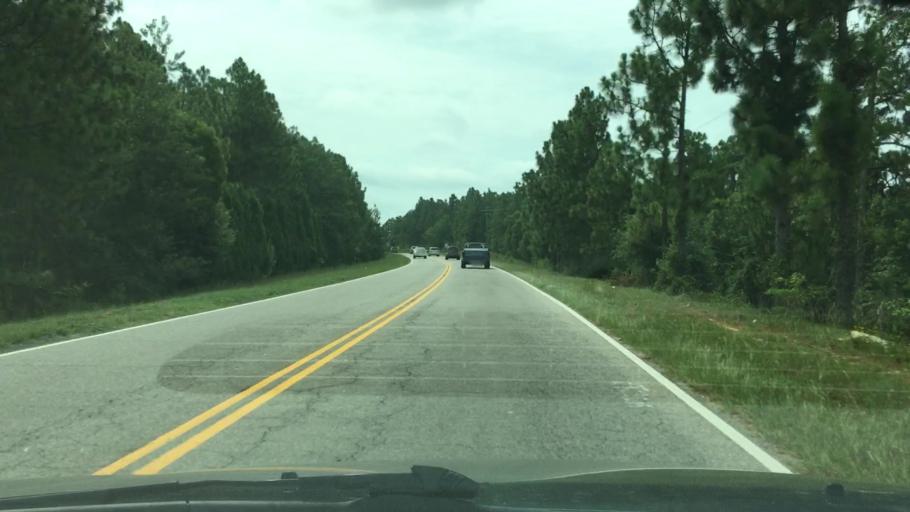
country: US
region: South Carolina
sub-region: Aiken County
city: Warrenville
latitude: 33.5327
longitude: -81.7716
